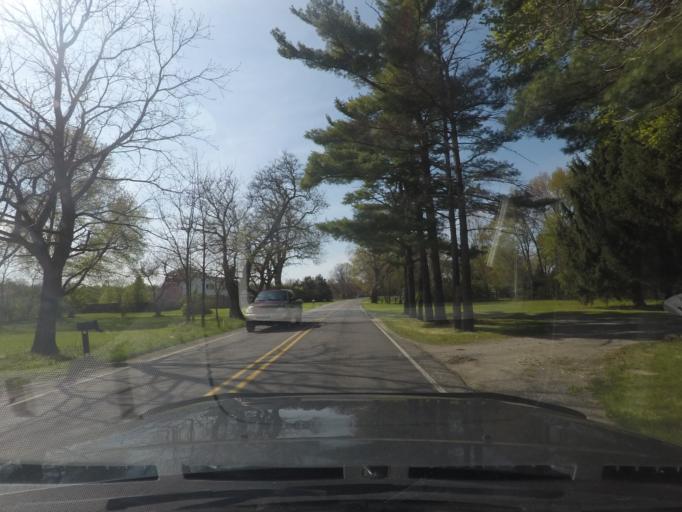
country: US
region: Indiana
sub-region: Elkhart County
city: Elkhart
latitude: 41.7124
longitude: -86.0270
